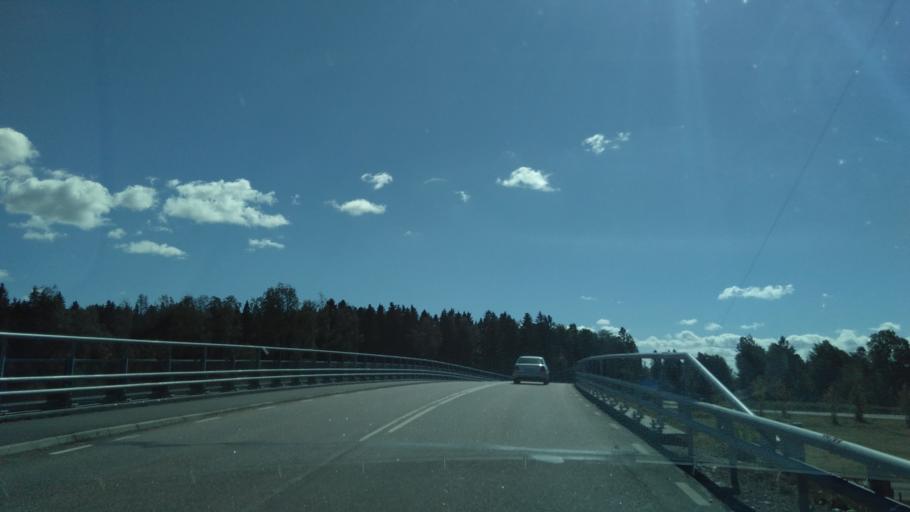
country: SE
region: Vaestra Goetaland
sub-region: Skara Kommun
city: Axvall
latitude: 58.3975
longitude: 13.5622
